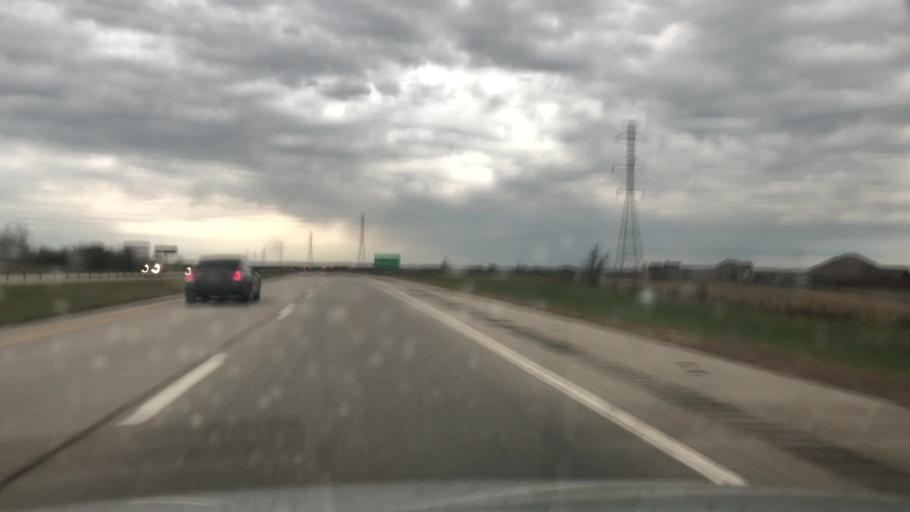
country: US
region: Oklahoma
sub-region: Tulsa County
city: Sperry
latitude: 36.3419
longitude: -95.9237
